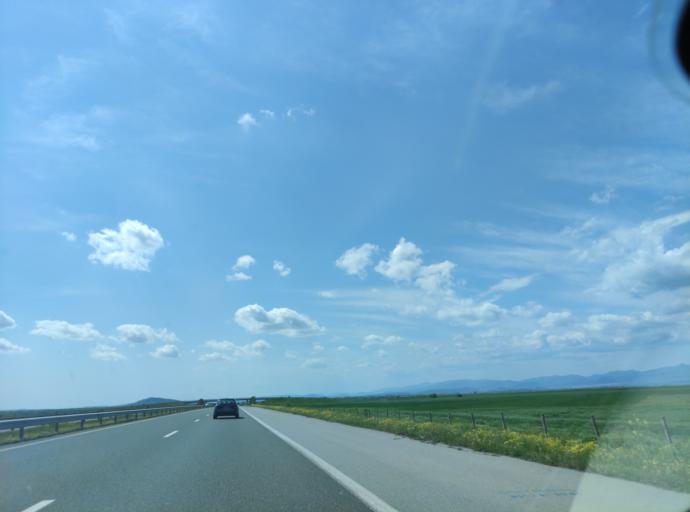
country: BG
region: Yambol
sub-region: Obshtina Yambol
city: Yambol
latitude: 42.5555
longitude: 26.5605
